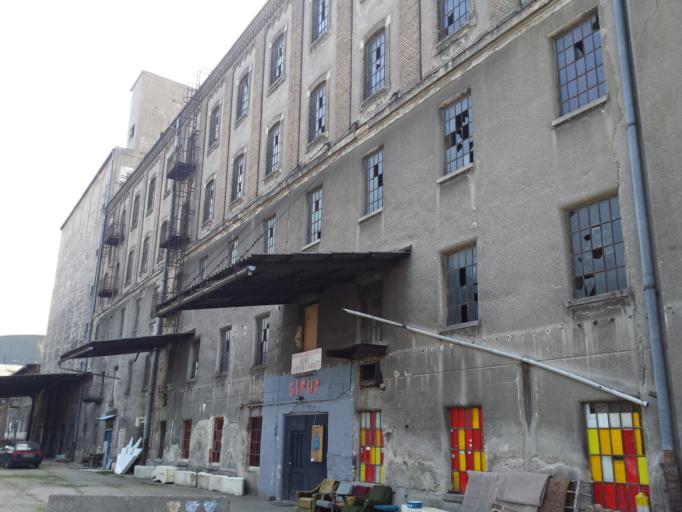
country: HR
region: Grad Zagreb
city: Zagreb - Centar
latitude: 45.8030
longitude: 15.9806
